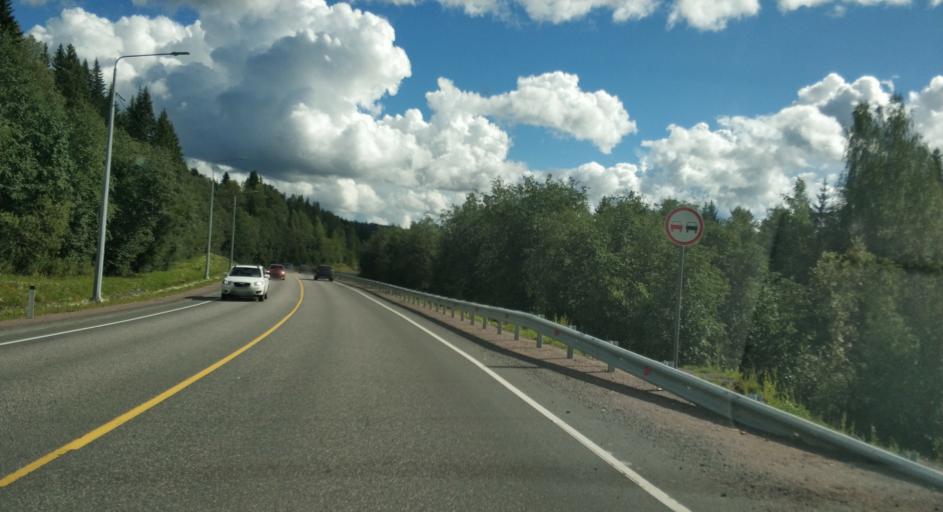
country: RU
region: Republic of Karelia
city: Ruskeala
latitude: 61.9221
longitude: 30.6112
